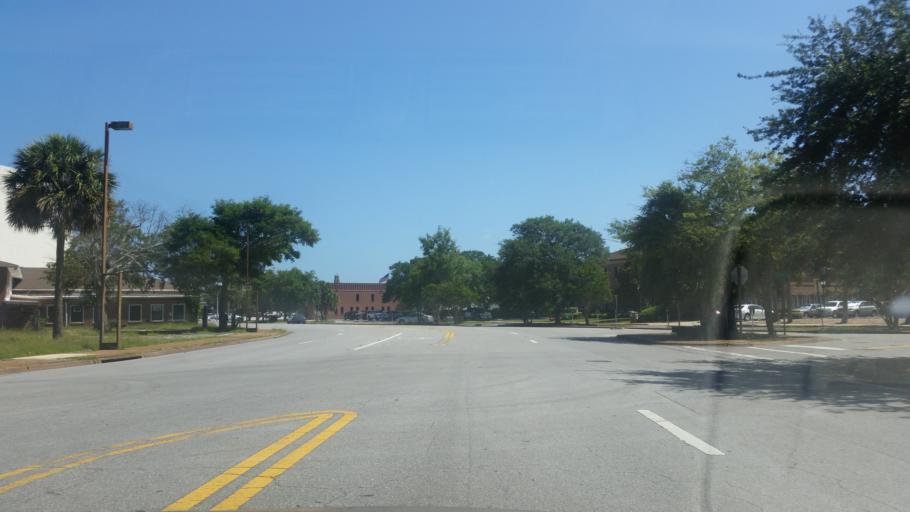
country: US
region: Florida
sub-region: Escambia County
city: Pensacola
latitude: 30.4107
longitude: -87.2180
